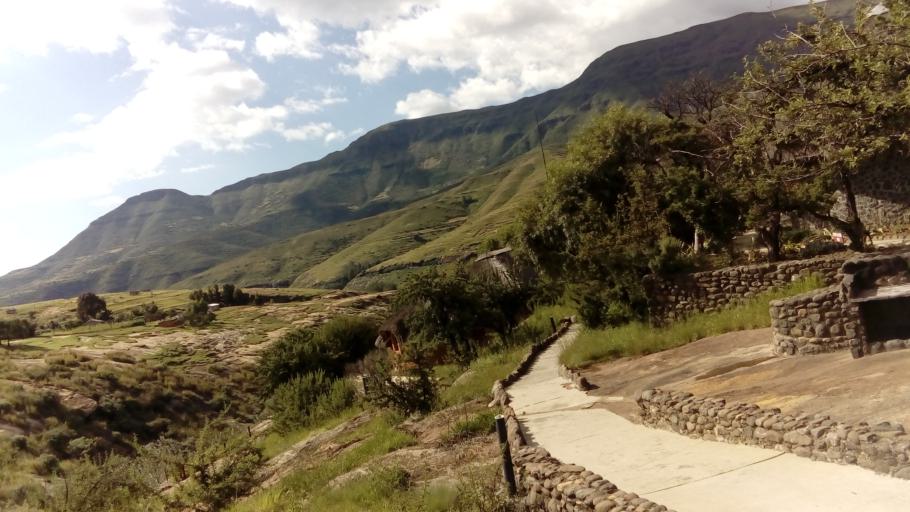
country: LS
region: Butha-Buthe
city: Butha-Buthe
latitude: -28.7538
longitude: 28.4950
